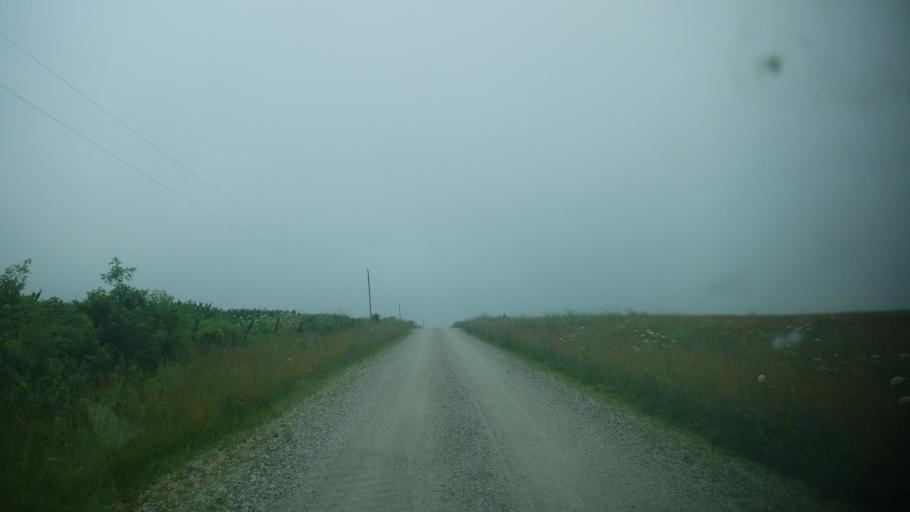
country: US
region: Missouri
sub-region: Audrain County
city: Vandalia
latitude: 39.2725
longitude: -91.3361
